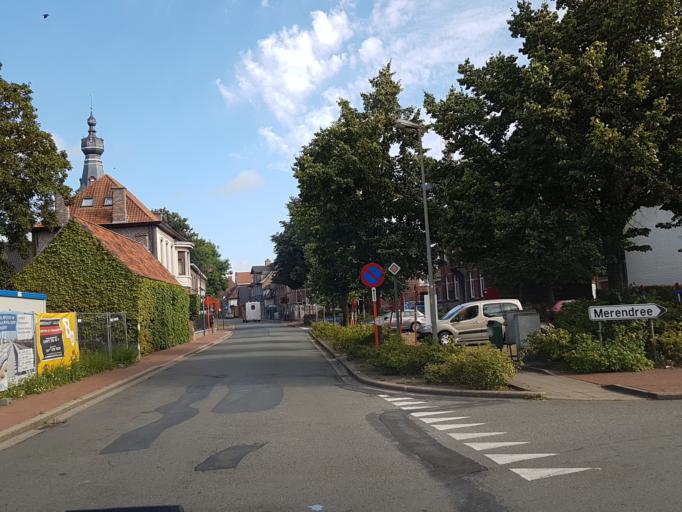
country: BE
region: Flanders
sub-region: Provincie Oost-Vlaanderen
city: Nevele
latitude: 51.0734
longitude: 3.5358
